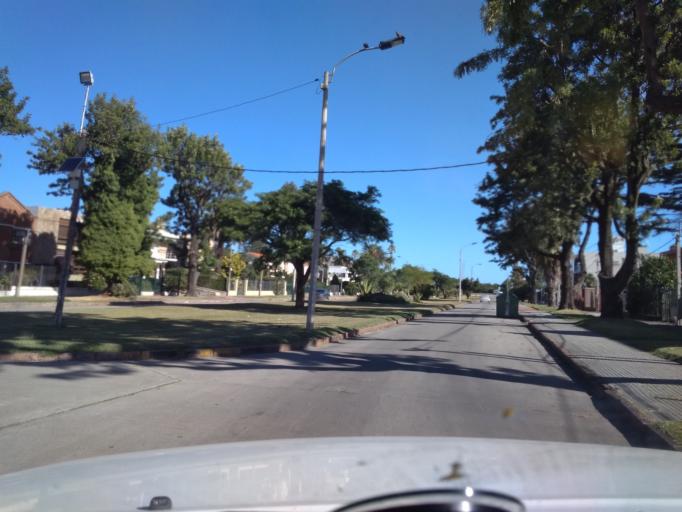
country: UY
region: Canelones
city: Paso de Carrasco
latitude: -34.8951
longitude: -56.0733
